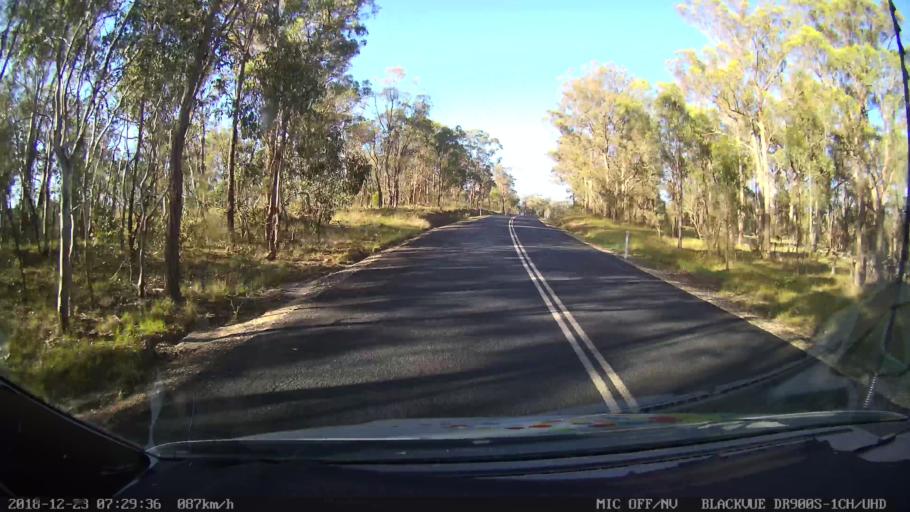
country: AU
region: New South Wales
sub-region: Armidale Dumaresq
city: Enmore
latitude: -30.4966
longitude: 152.1544
